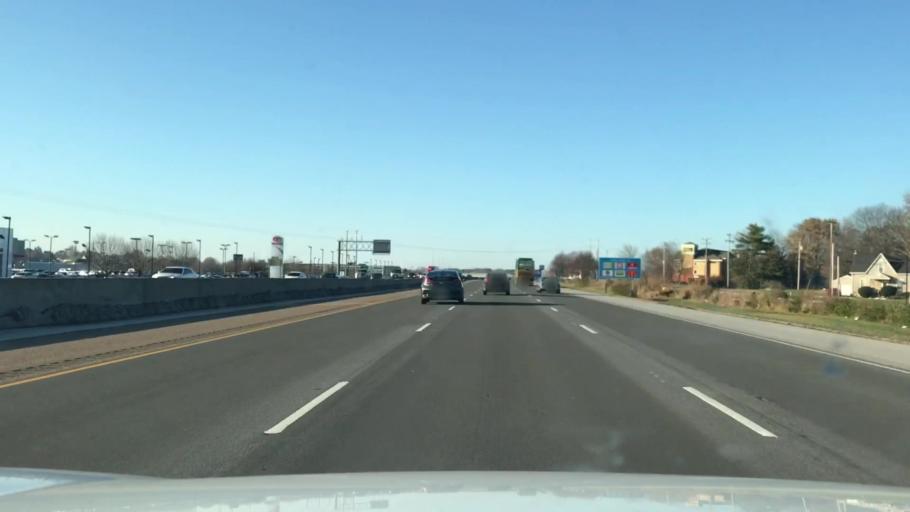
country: US
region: Illinois
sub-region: Saint Clair County
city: O'Fallon
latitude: 38.5839
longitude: -89.9376
